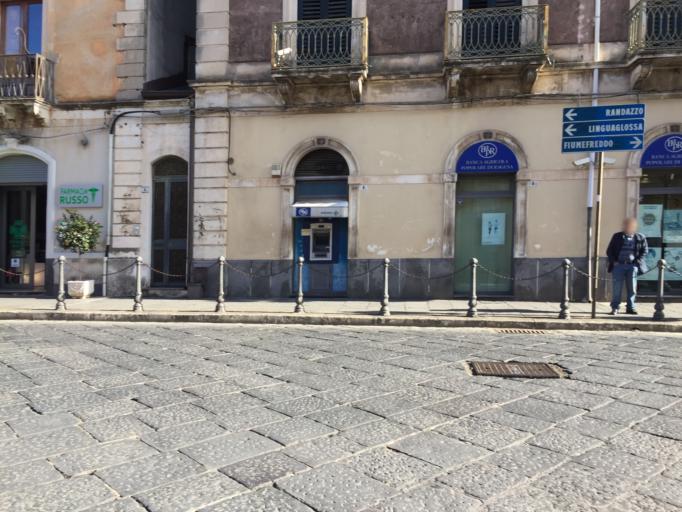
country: IT
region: Sicily
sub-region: Catania
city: Piedimonte Etneo
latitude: 37.8071
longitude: 15.1785
